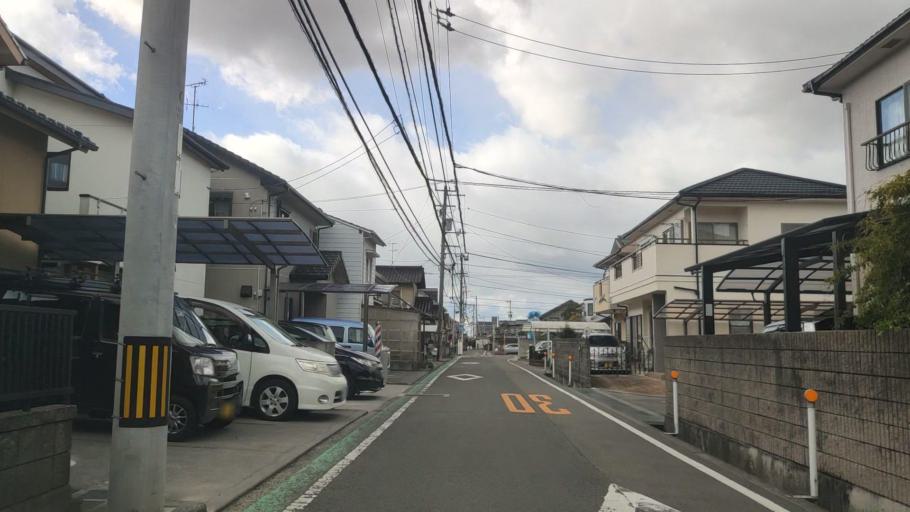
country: JP
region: Ehime
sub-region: Shikoku-chuo Shi
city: Matsuyama
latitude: 33.8098
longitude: 132.7866
